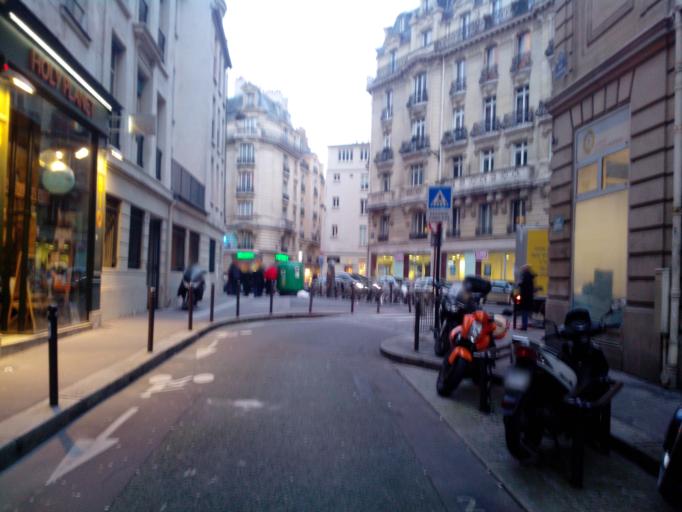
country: FR
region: Ile-de-France
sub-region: Paris
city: Paris
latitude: 48.8524
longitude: 2.3411
